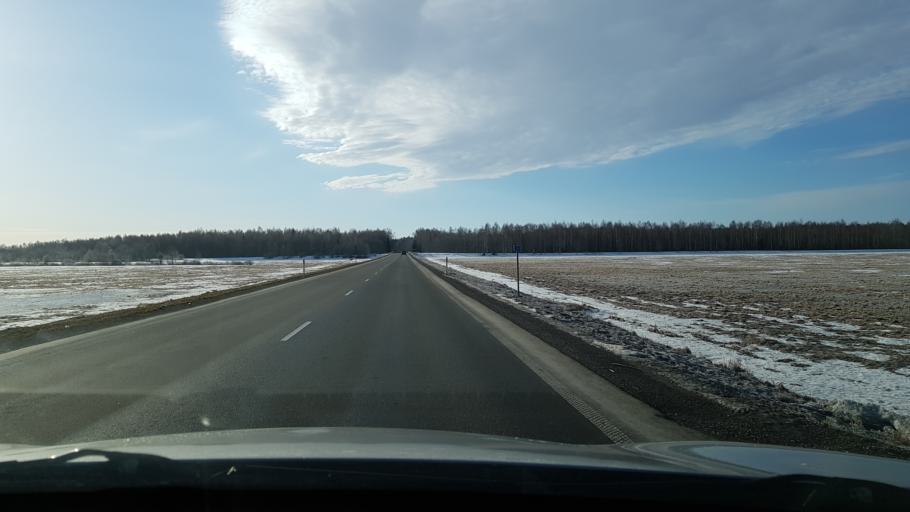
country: EE
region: Viljandimaa
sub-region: Vohma linn
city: Vohma
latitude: 58.5883
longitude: 25.5710
